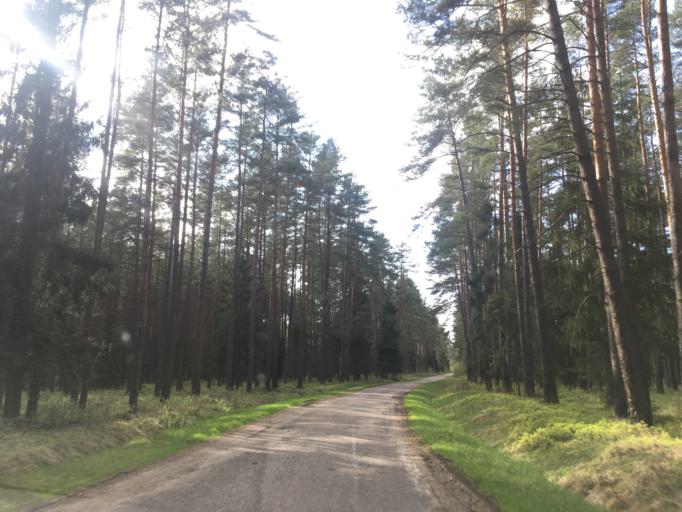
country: PL
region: Warmian-Masurian Voivodeship
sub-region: Powiat nidzicki
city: Nidzica
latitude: 53.4371
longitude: 20.5305
